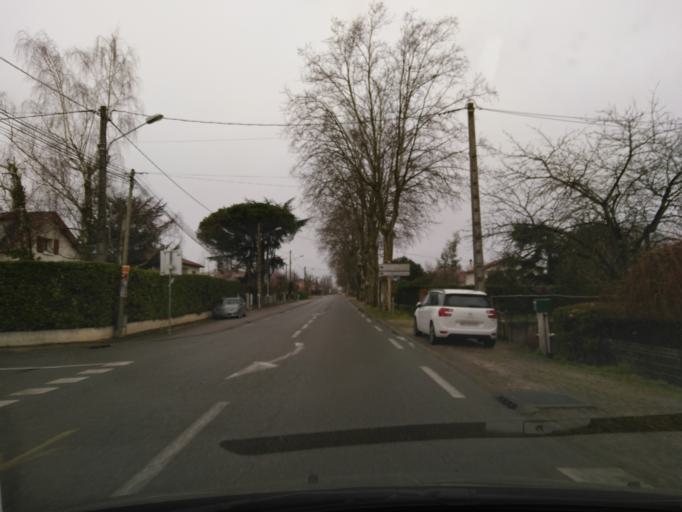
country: FR
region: Midi-Pyrenees
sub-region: Departement de la Haute-Garonne
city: Rieux-Volvestre
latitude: 43.2602
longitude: 1.1934
